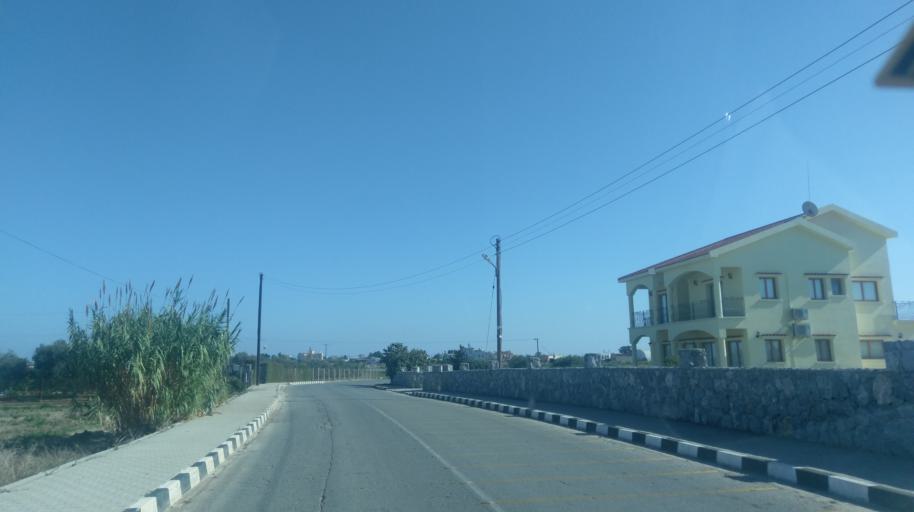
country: CY
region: Ammochostos
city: Trikomo
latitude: 35.2364
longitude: 33.8655
